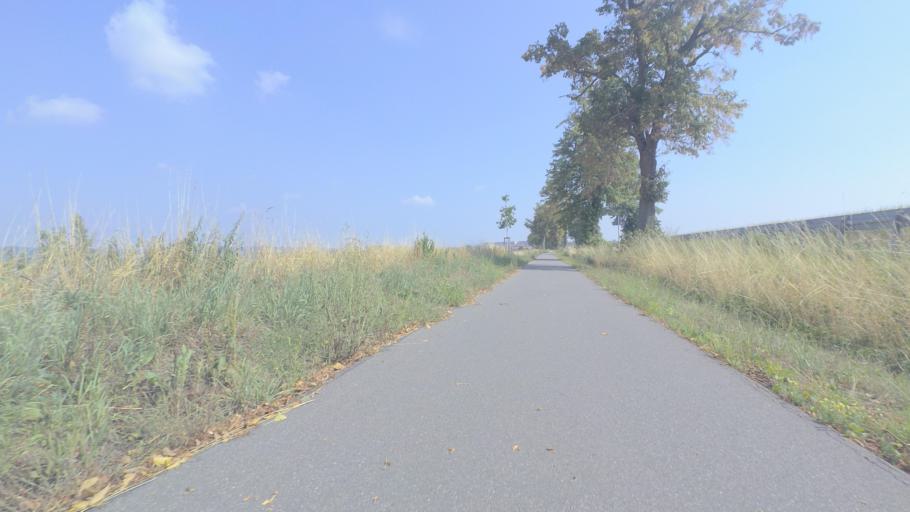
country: DE
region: Mecklenburg-Vorpommern
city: Gielow
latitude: 53.7280
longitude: 12.7294
